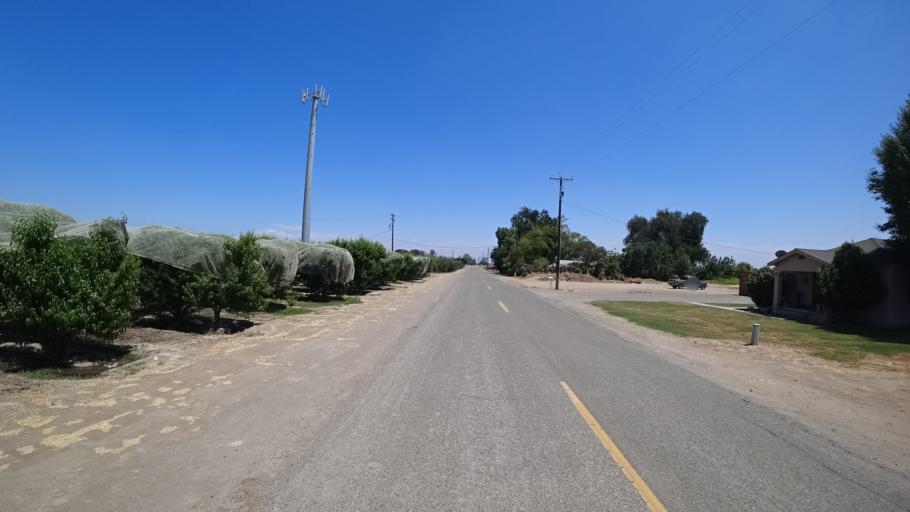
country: US
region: California
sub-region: Kings County
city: Lucerne
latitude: 36.3865
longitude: -119.6422
